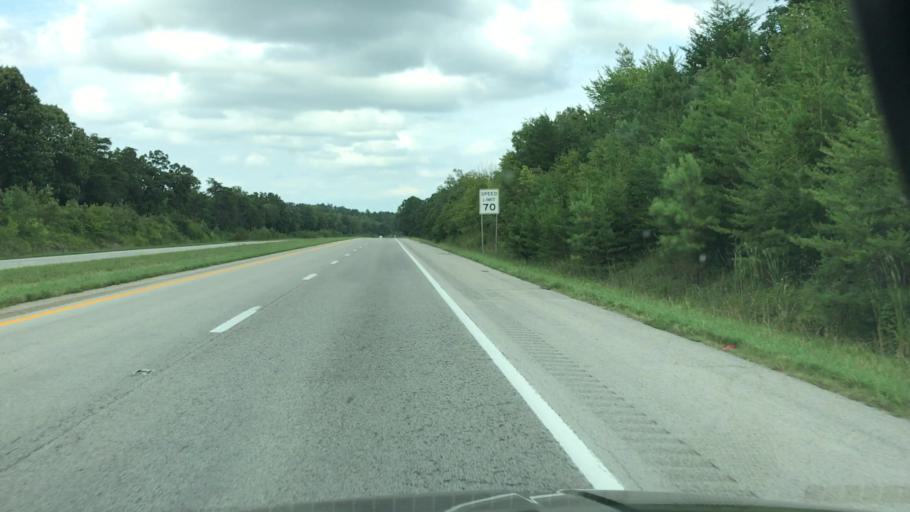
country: US
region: Kentucky
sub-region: Caldwell County
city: Princeton
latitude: 37.1475
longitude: -87.7990
